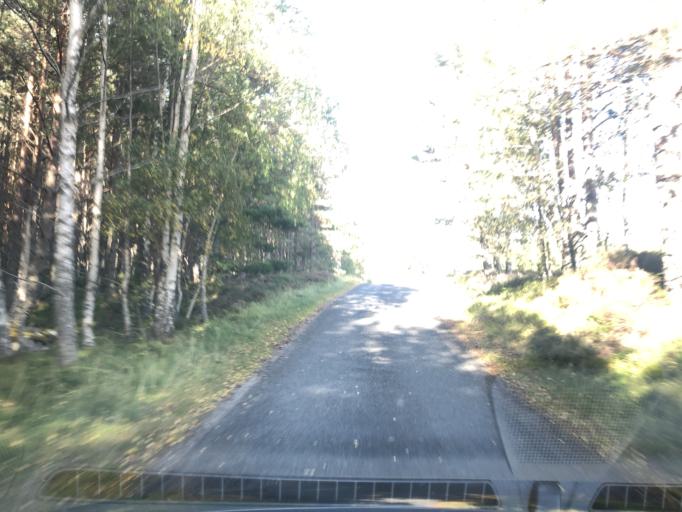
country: GB
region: Scotland
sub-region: Highland
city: Aviemore
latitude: 57.0737
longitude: -3.9020
